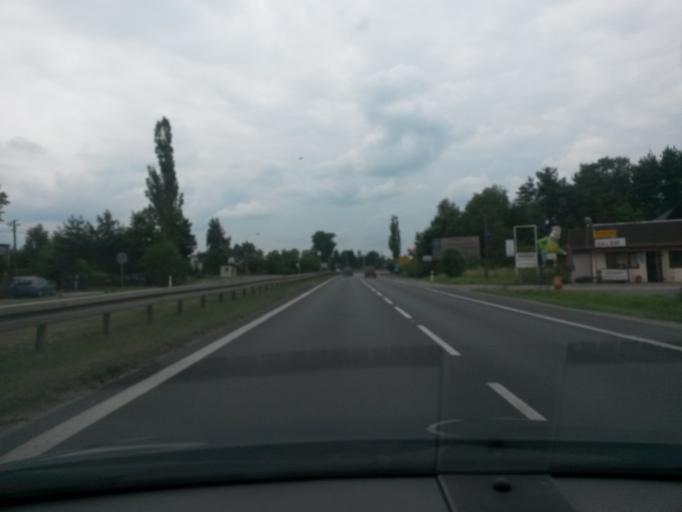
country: PL
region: Masovian Voivodeship
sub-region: Powiat pruszkowski
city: Nadarzyn
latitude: 52.0796
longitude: 20.7876
